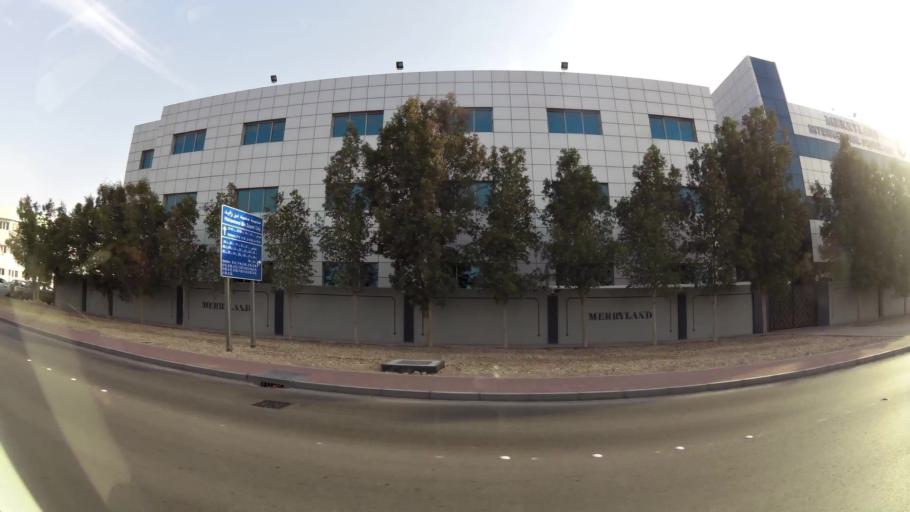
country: AE
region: Abu Dhabi
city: Abu Dhabi
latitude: 24.3472
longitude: 54.5358
